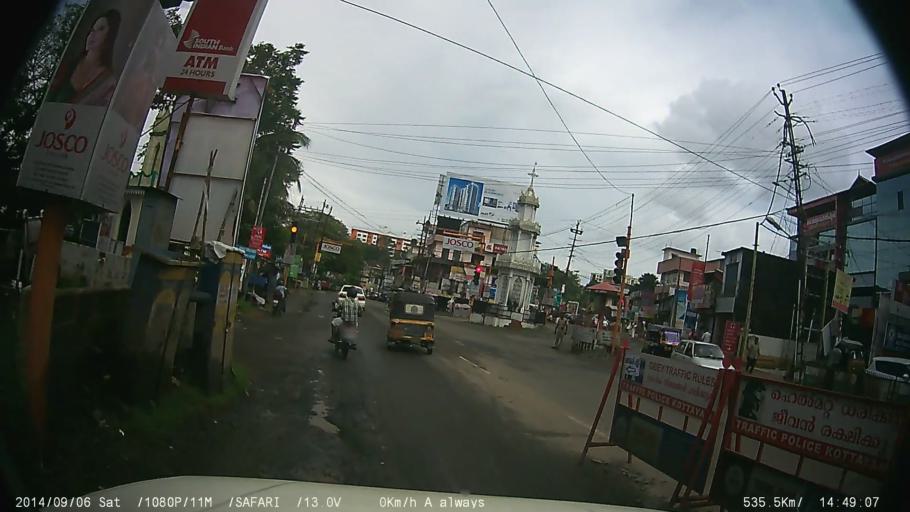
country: IN
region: Kerala
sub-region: Kottayam
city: Kottayam
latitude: 9.5875
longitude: 76.5427
